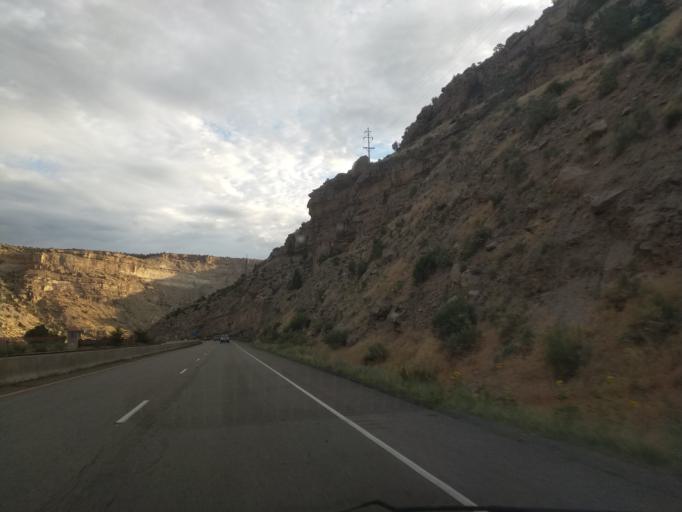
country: US
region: Colorado
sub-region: Mesa County
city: Palisade
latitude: 39.1869
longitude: -108.2804
